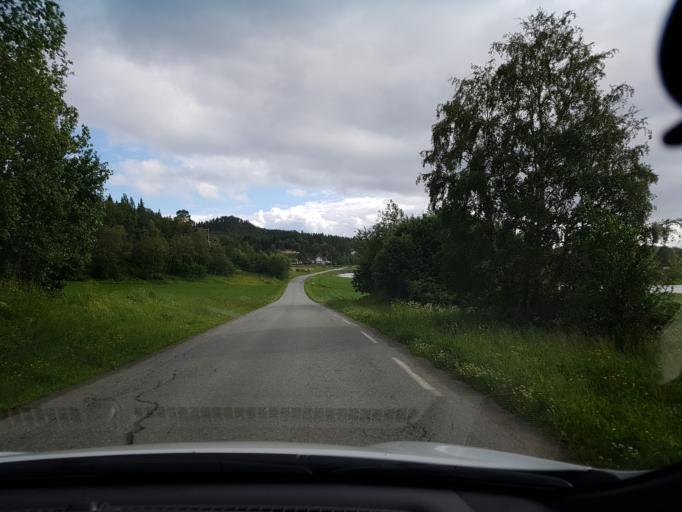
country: NO
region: Nord-Trondelag
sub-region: Frosta
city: Frosta
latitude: 63.6266
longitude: 10.7652
